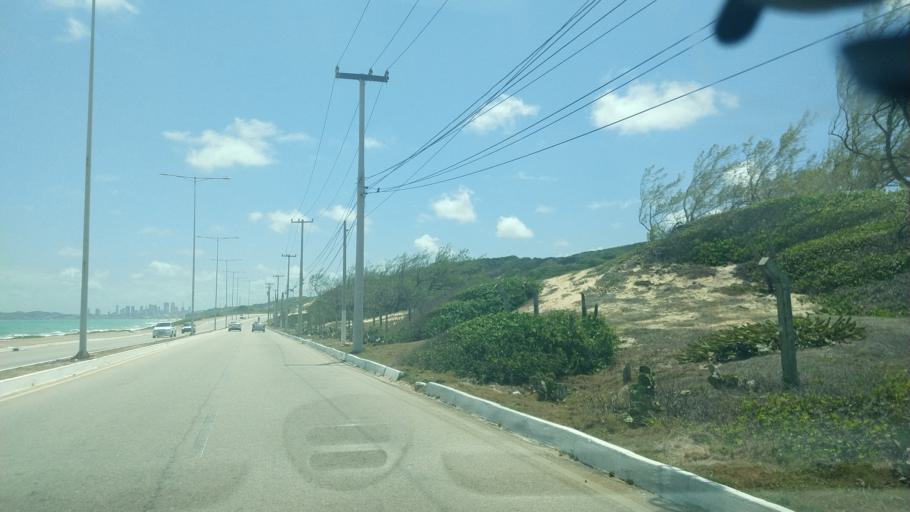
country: BR
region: Rio Grande do Norte
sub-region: Natal
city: Natal
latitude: -5.8119
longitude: -35.1820
